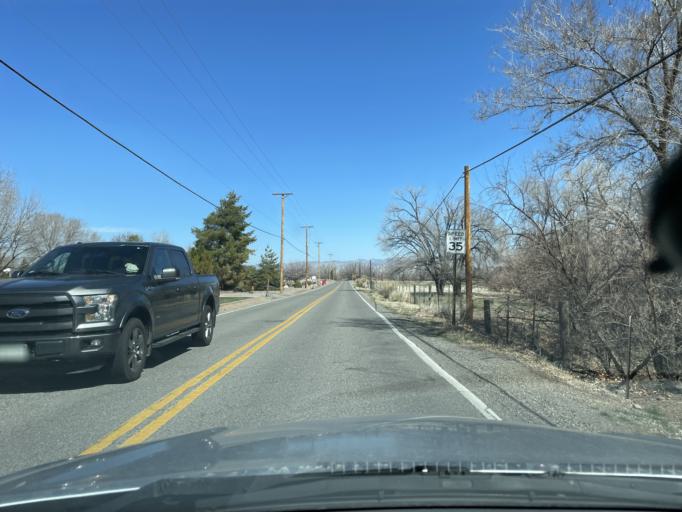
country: US
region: Colorado
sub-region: Mesa County
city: Redlands
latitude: 39.0854
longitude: -108.6687
